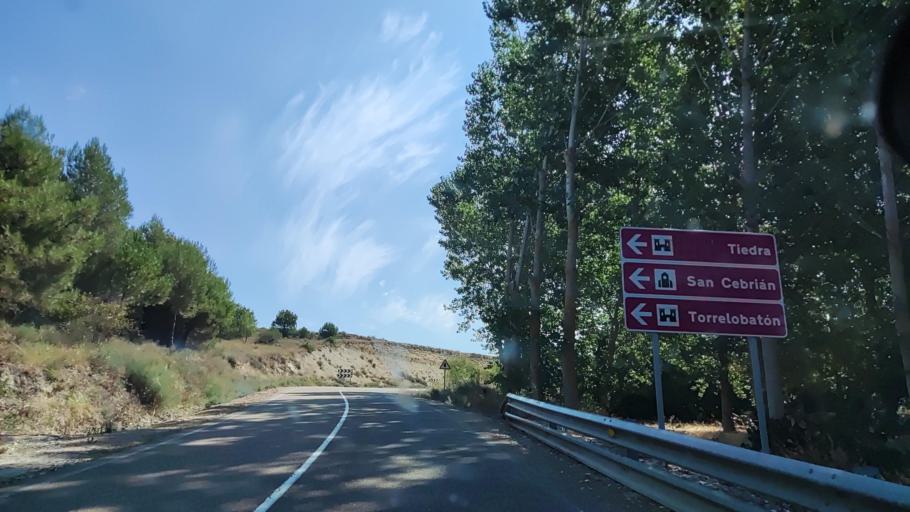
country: ES
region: Castille and Leon
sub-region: Provincia de Valladolid
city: Uruena
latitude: 41.7111
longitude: -5.1939
